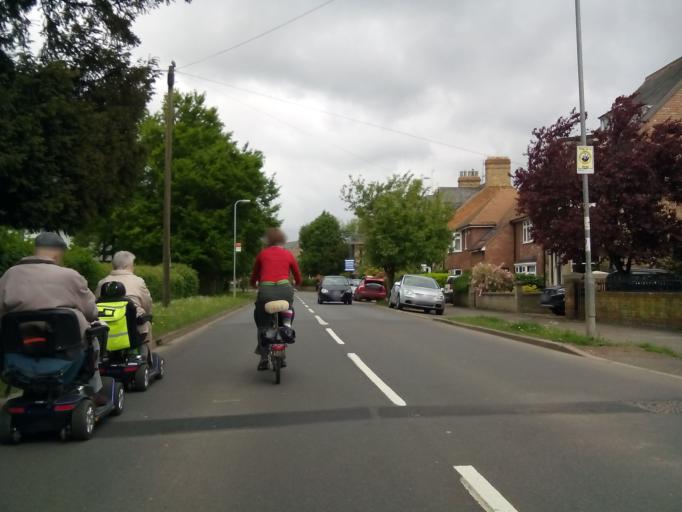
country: GB
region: England
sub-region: Northamptonshire
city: Oundle
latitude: 52.4867
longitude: -0.4728
